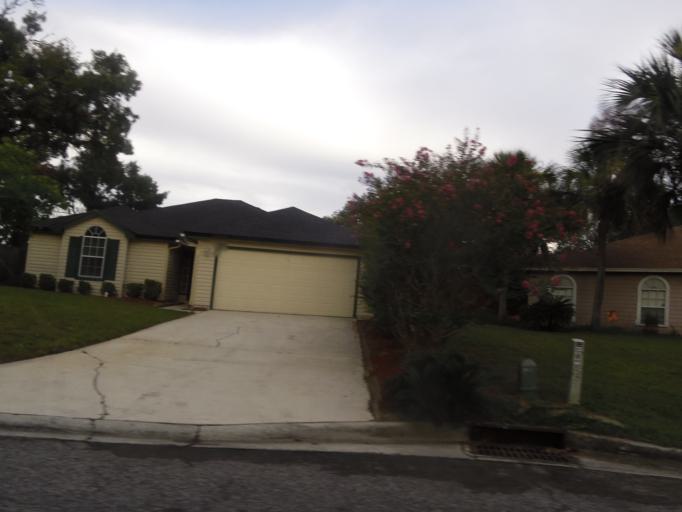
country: US
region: Florida
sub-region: Duval County
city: Atlantic Beach
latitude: 30.3655
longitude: -81.4989
